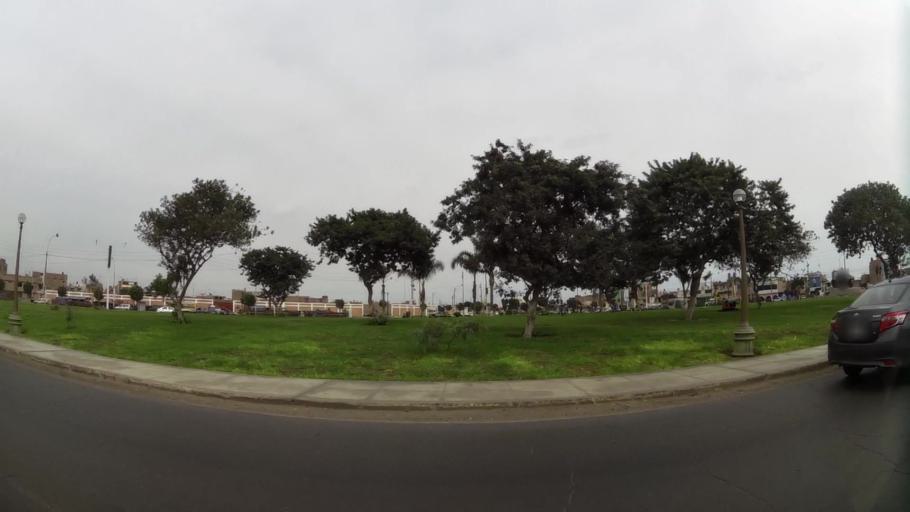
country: PE
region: Callao
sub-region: Callao
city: Callao
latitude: -11.9997
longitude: -77.1167
